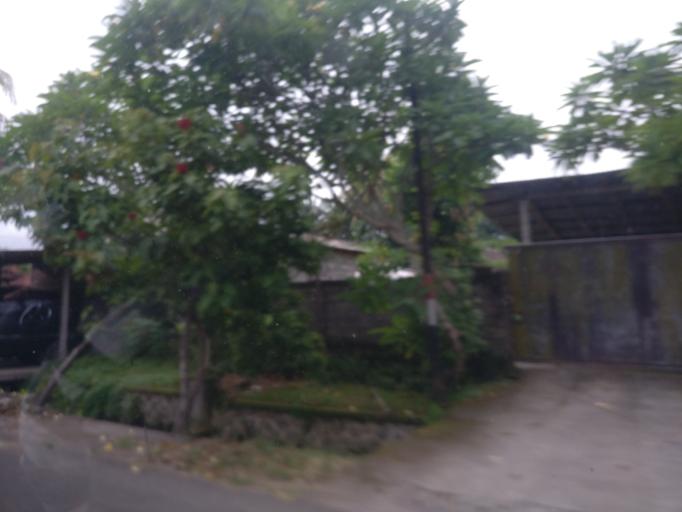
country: ID
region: Bali
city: Banjar Desa
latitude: -8.5754
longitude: 115.2963
